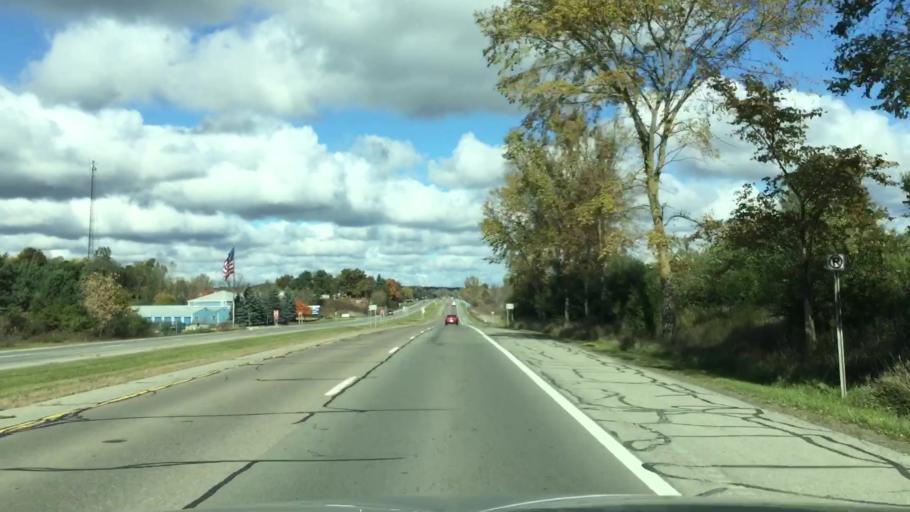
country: US
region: Michigan
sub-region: Oakland County
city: Oxford
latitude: 42.8543
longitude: -83.2842
